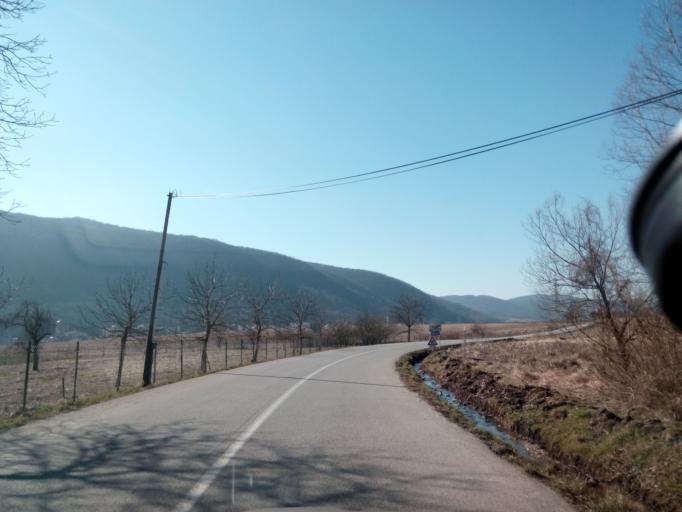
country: SK
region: Kosicky
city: Roznava
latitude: 48.5892
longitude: 20.6705
